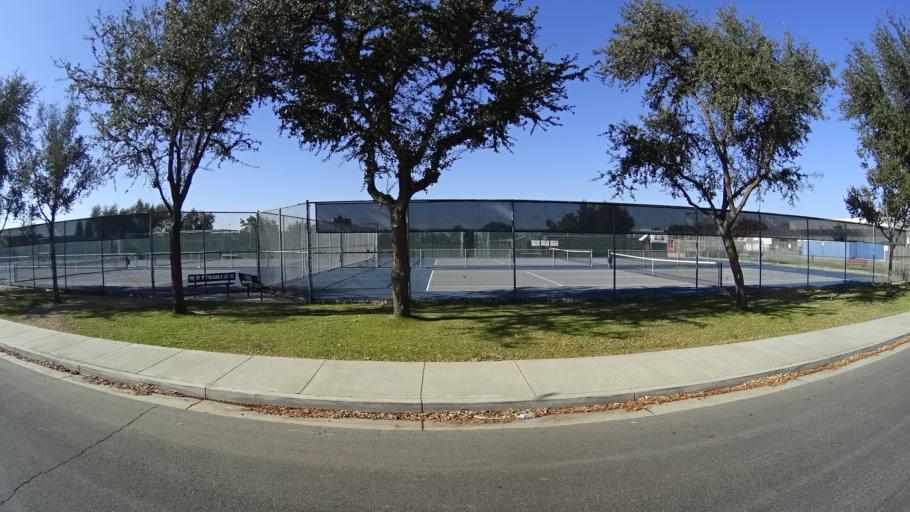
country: US
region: California
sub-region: Kern County
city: Rosedale
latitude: 35.3644
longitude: -119.1280
